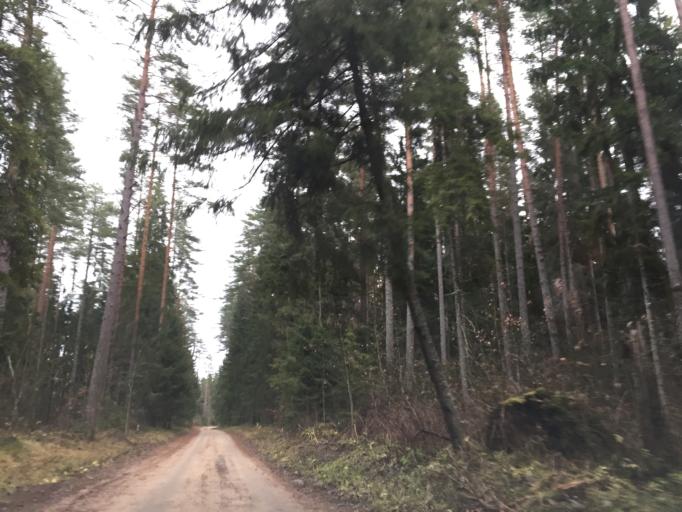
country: LV
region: Valmieras Rajons
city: Valmiera
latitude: 57.5521
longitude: 25.4798
